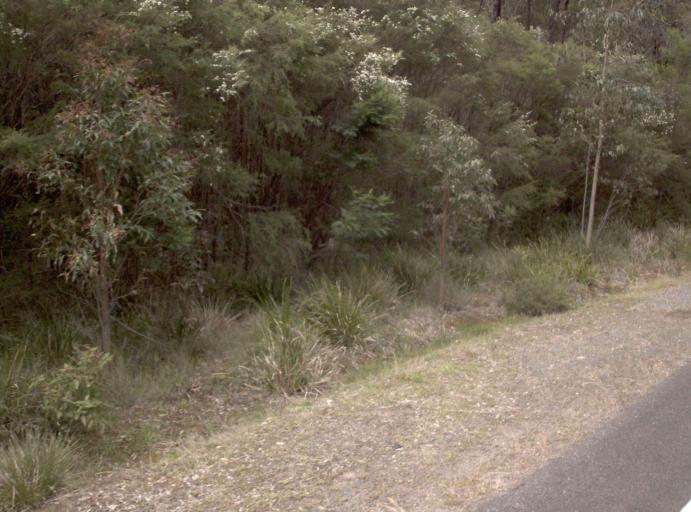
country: AU
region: New South Wales
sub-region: Bega Valley
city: Eden
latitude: -37.4575
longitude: 149.6122
